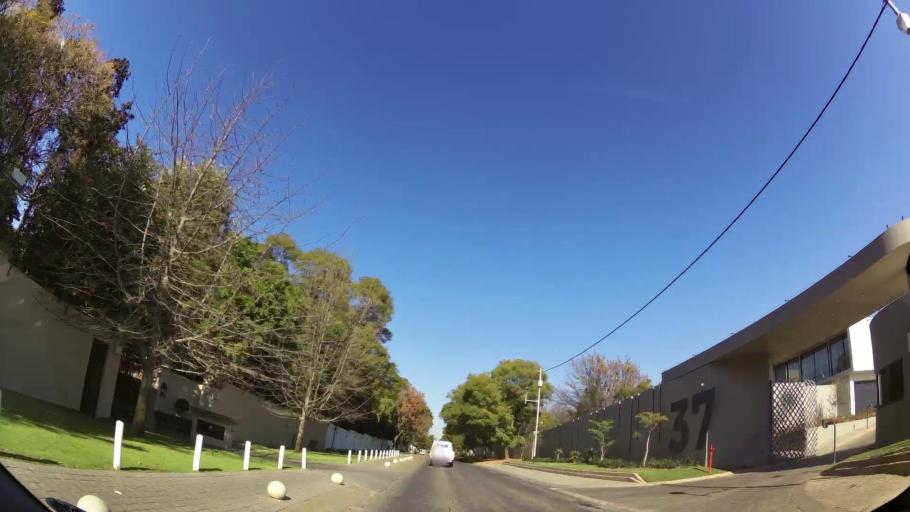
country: ZA
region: Gauteng
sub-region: City of Johannesburg Metropolitan Municipality
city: Midrand
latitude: -26.0604
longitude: 28.0292
